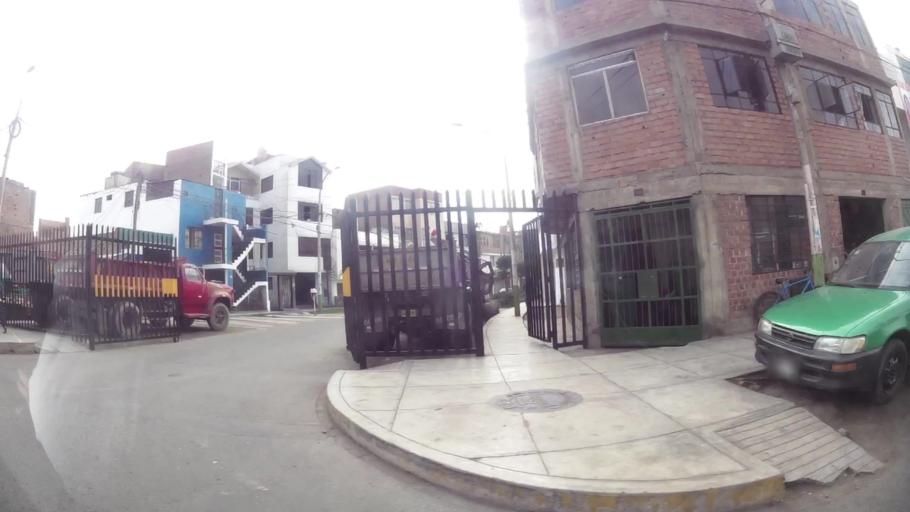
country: PE
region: Callao
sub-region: Callao
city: Callao
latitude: -12.0228
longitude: -77.0982
